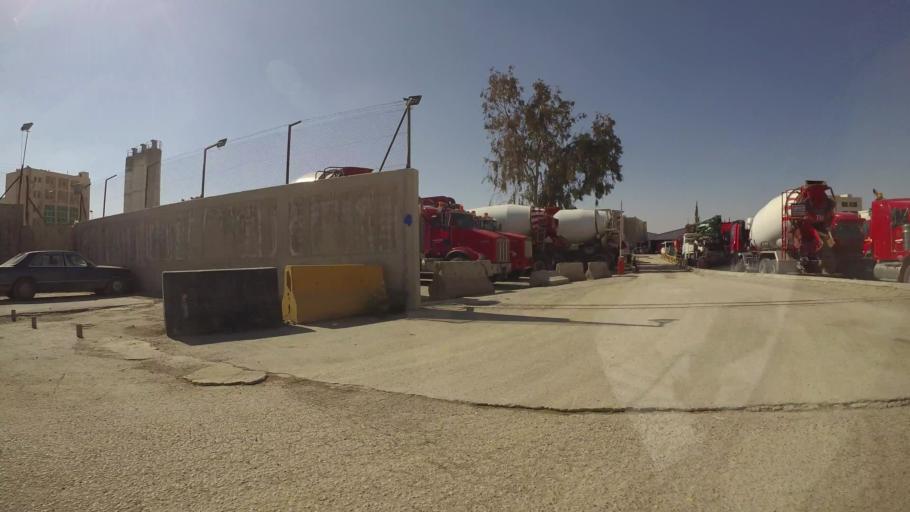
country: JO
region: Amman
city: Al Bunayyat ash Shamaliyah
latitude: 31.9132
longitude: 35.9131
